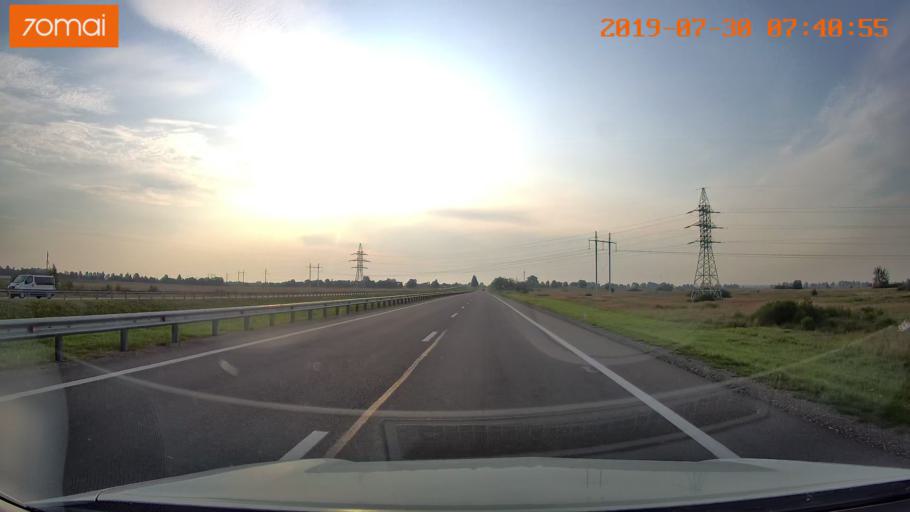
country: RU
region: Kaliningrad
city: Gvardeysk
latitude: 54.6484
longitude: 21.2356
